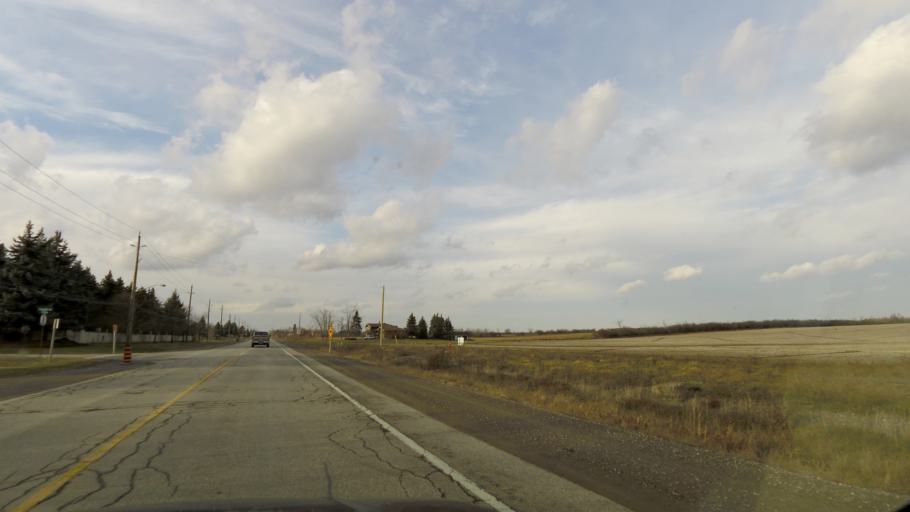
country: CA
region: Ontario
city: Brampton
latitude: 43.8024
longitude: -79.7041
